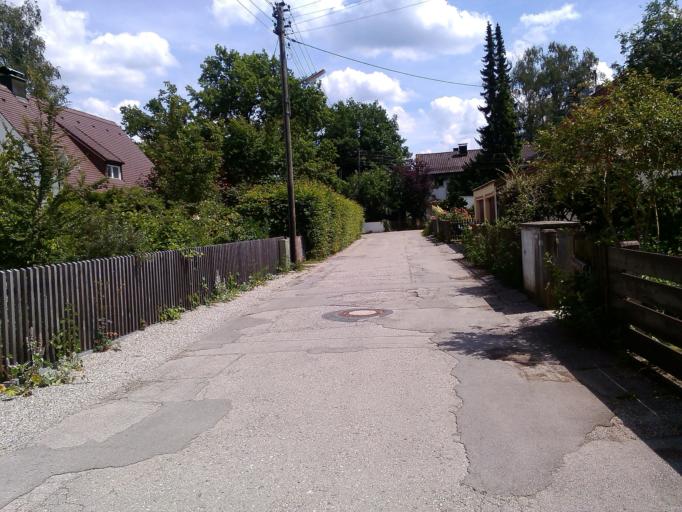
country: DE
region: Bavaria
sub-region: Upper Bavaria
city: Gauting
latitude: 48.0724
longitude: 11.3633
